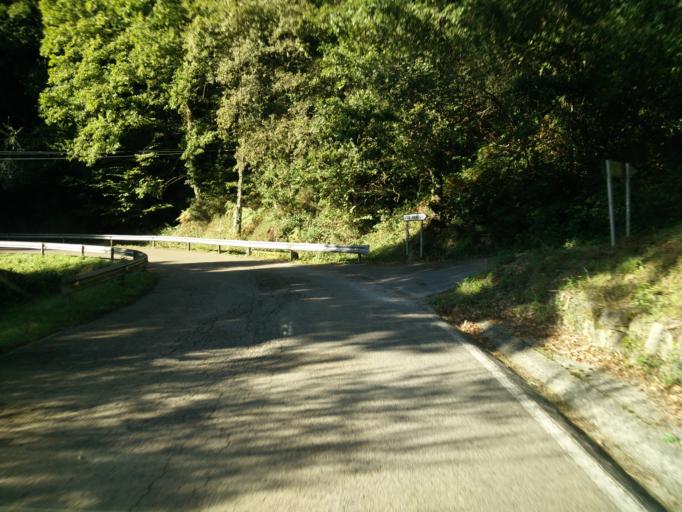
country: ES
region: Cantabria
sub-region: Provincia de Cantabria
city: San Pedro del Romeral
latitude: 43.1345
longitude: -3.8157
